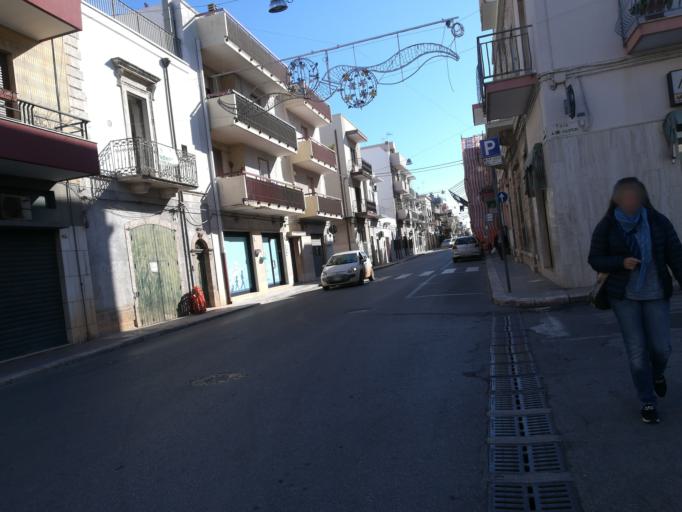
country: IT
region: Apulia
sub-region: Provincia di Bari
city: Polignano a Mare
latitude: 40.9929
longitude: 17.2234
